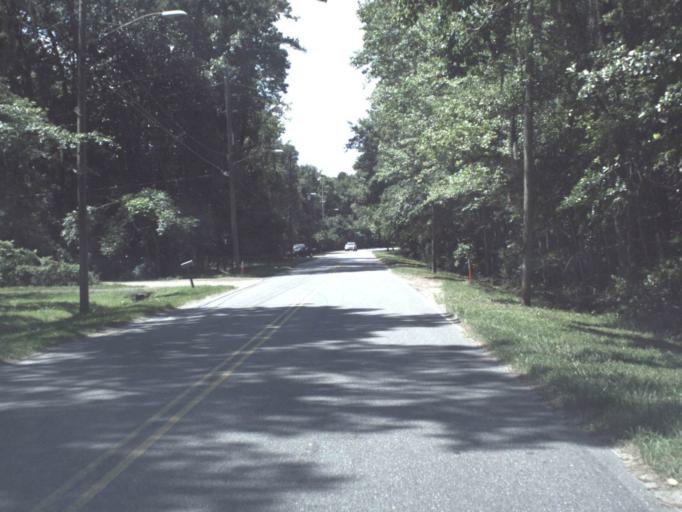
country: US
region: Florida
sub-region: Duval County
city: Jacksonville
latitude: 30.3678
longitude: -81.7337
